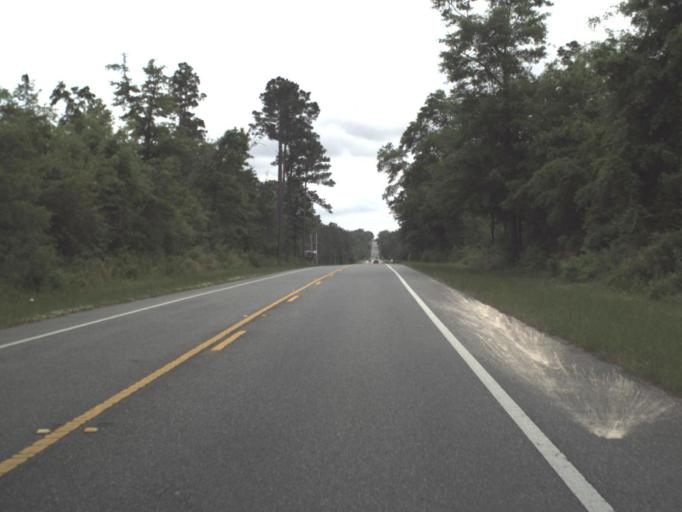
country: US
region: Florida
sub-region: Santa Rosa County
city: Point Baker
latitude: 30.7957
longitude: -87.0413
